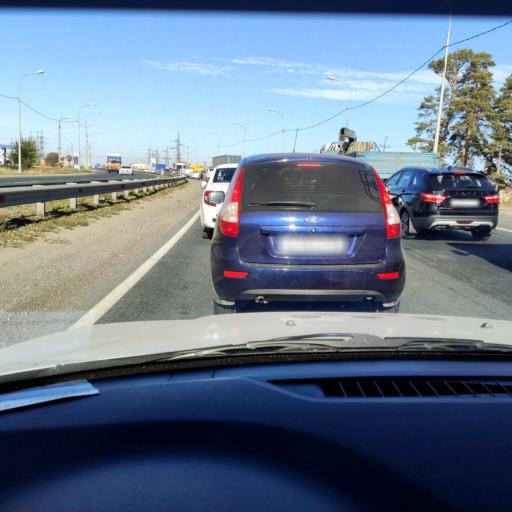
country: RU
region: Samara
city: Zhigulevsk
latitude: 53.5391
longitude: 49.5166
